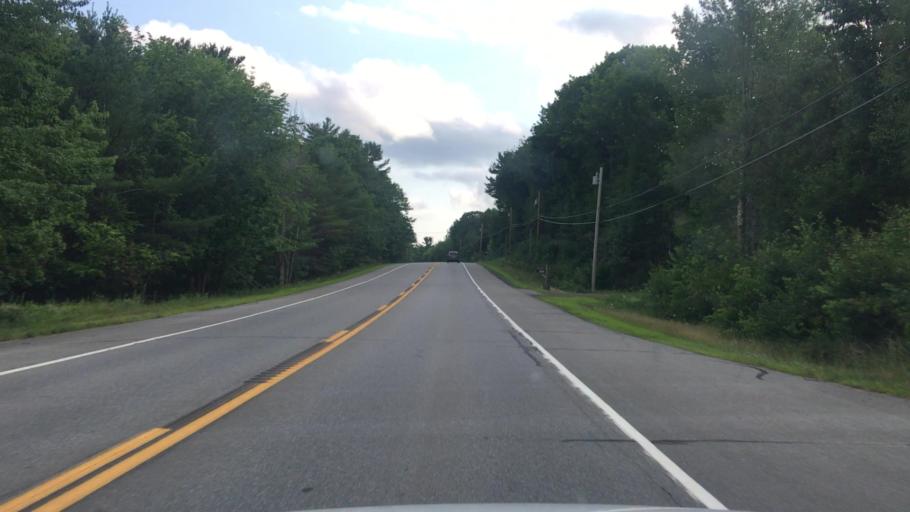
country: US
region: Maine
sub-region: Kennebec County
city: Windsor
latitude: 44.3601
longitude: -69.6406
